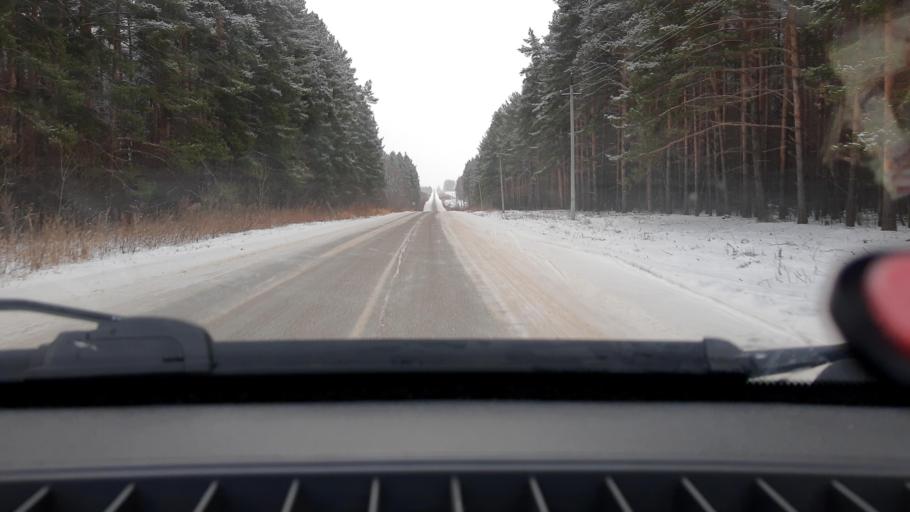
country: RU
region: Bashkortostan
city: Iglino
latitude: 54.6790
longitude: 56.4178
